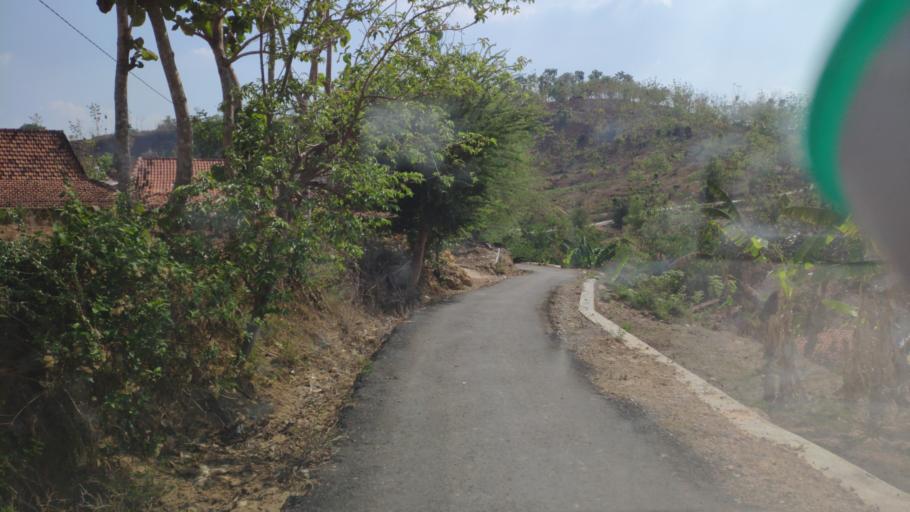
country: ID
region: Central Java
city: Ngapus
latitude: -6.9303
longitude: 111.2179
